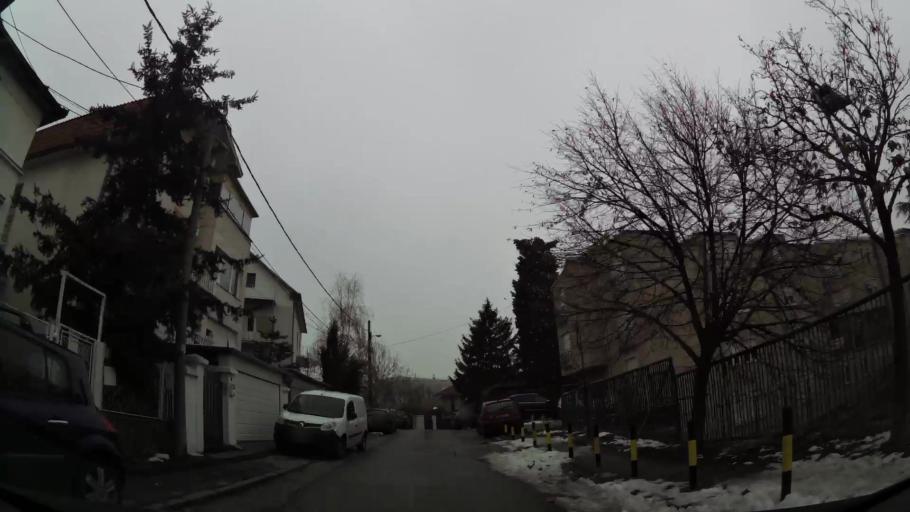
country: RS
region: Central Serbia
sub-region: Belgrade
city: Vozdovac
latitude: 44.7805
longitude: 20.4779
